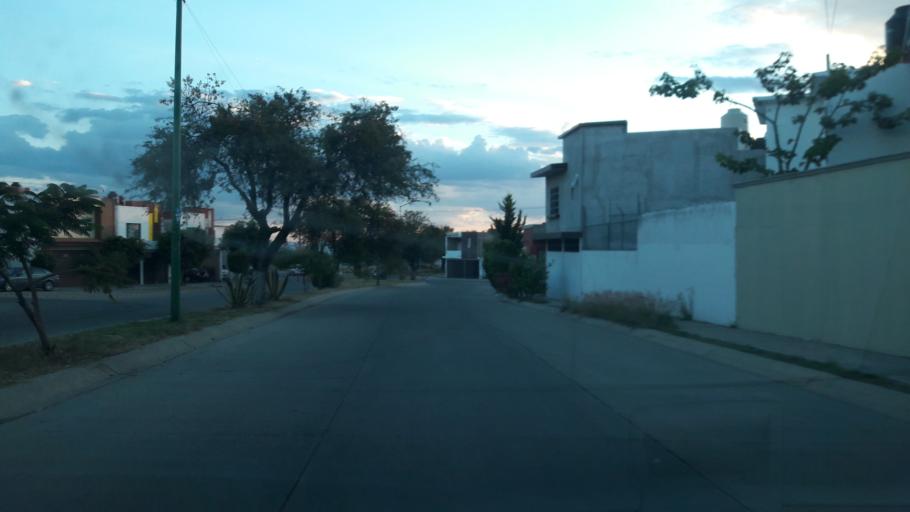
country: MX
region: Guanajuato
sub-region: Leon
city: Medina
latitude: 21.1658
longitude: -101.6318
